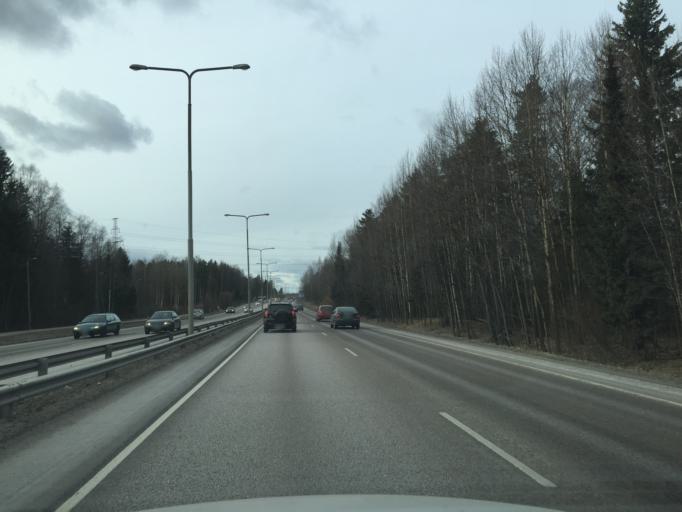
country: FI
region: Uusimaa
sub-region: Helsinki
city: Teekkarikylae
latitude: 60.2551
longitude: 24.8815
